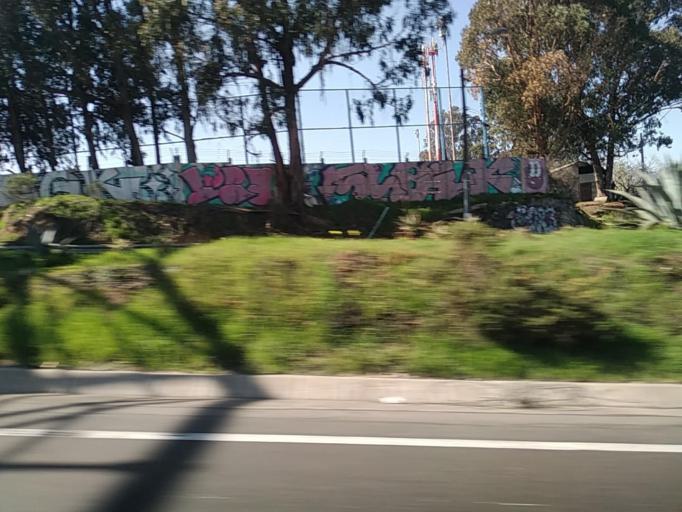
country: CL
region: Valparaiso
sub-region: Provincia de Valparaiso
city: Vina del Mar
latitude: -33.0354
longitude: -71.5016
